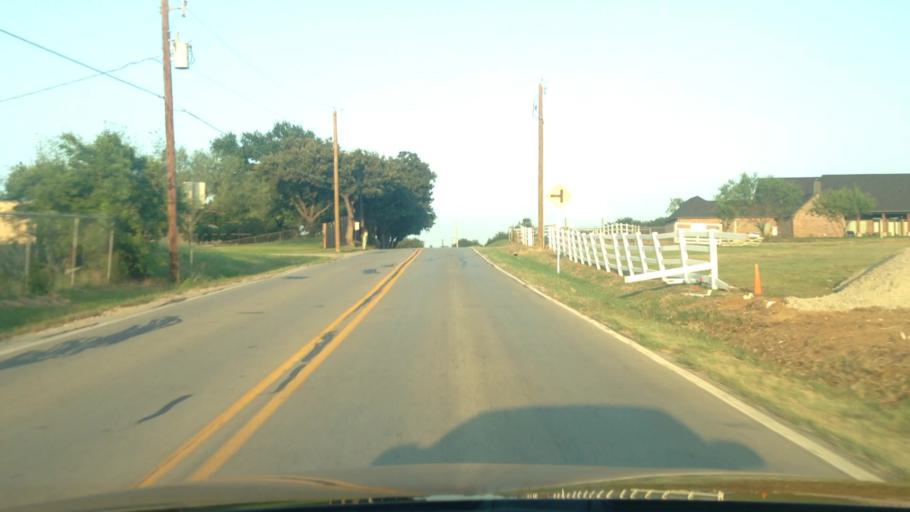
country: US
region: Texas
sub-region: Tarrant County
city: Kennedale
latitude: 32.6070
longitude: -97.2098
